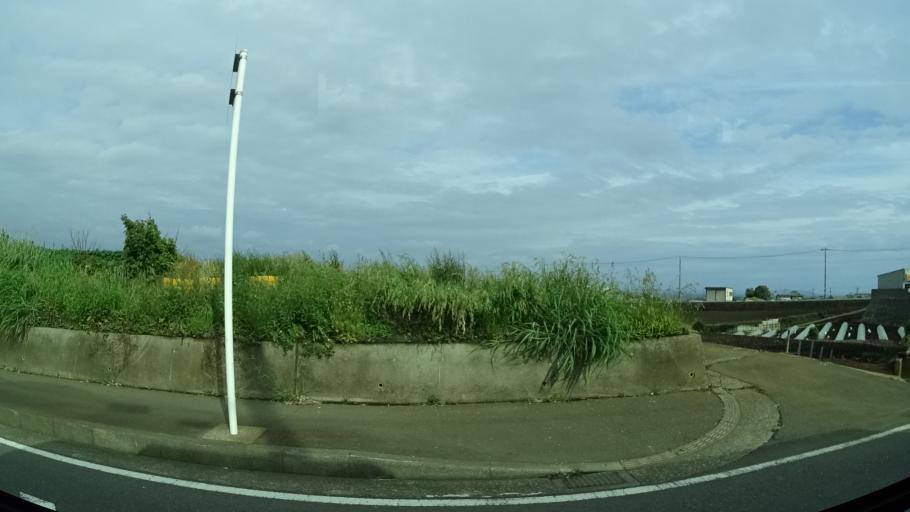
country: JP
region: Kanagawa
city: Miura
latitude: 35.1537
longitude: 139.6688
